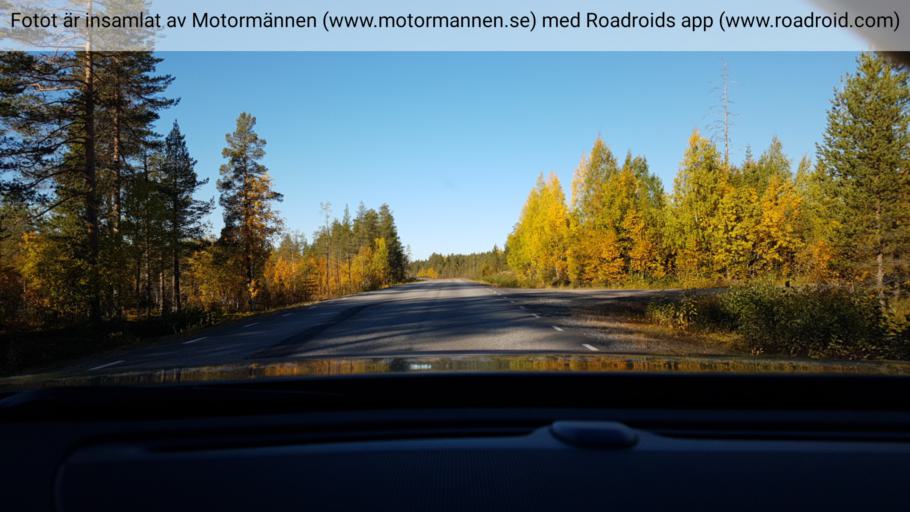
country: SE
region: Vaesterbotten
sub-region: Skelleftea Kommun
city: Storvik
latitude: 65.3286
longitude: 20.6607
